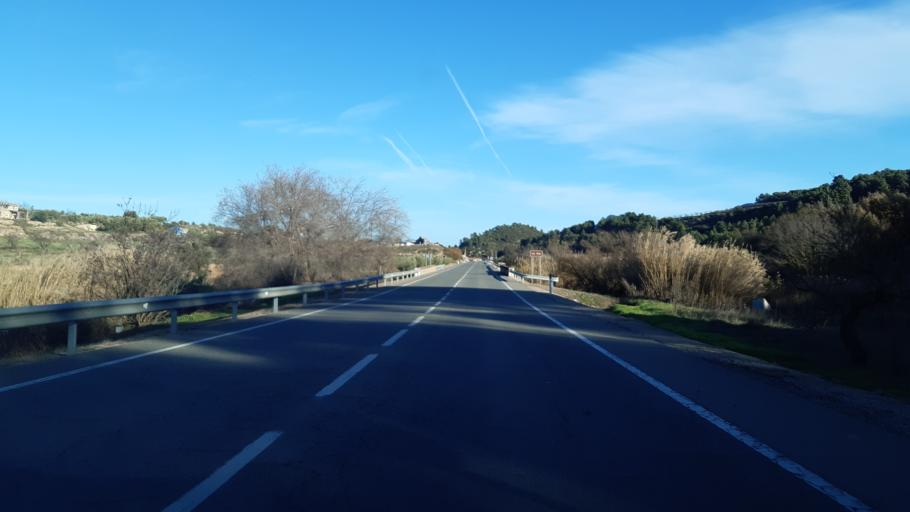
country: ES
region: Catalonia
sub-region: Provincia de Tarragona
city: Gandesa
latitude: 41.0695
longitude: 0.4544
